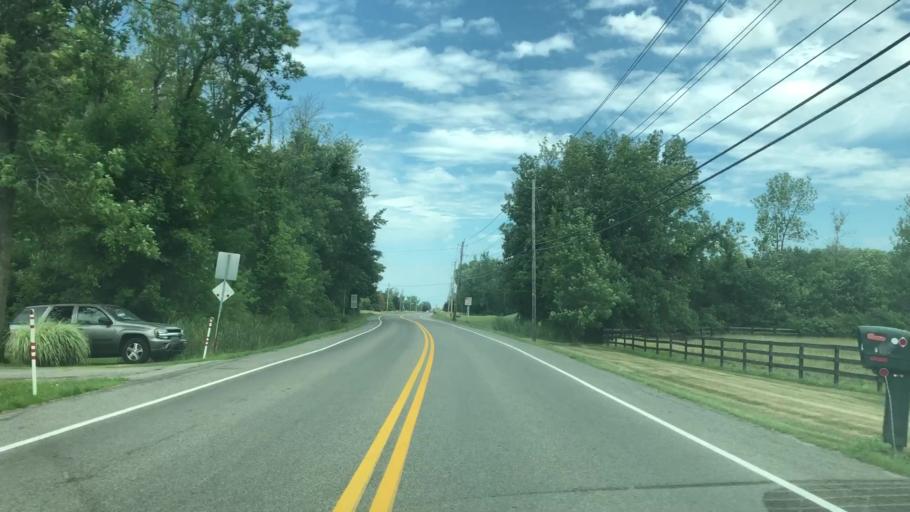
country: US
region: New York
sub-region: Monroe County
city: Webster
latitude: 43.1955
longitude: -77.4003
